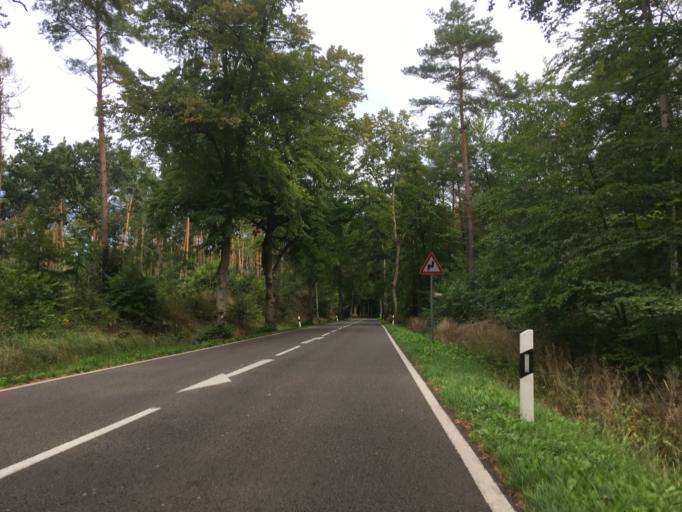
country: DE
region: Brandenburg
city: Templin
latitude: 53.1499
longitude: 13.5491
